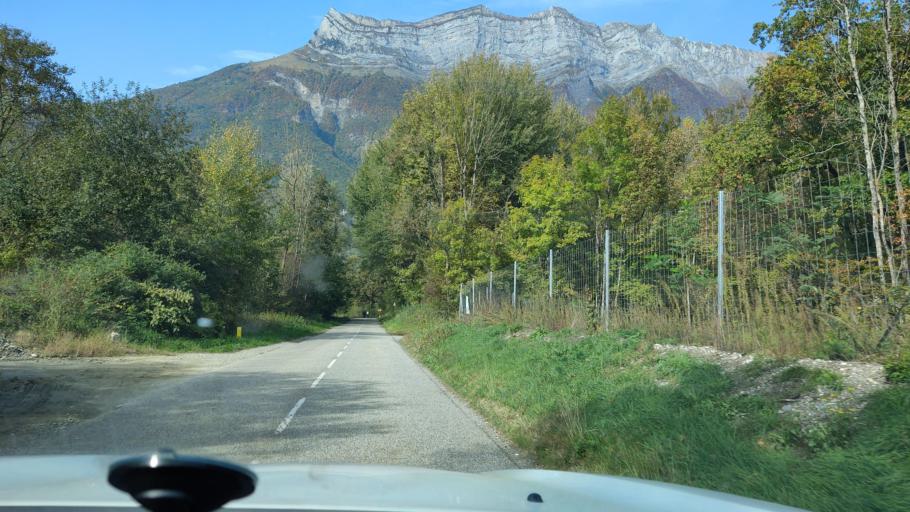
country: FR
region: Rhone-Alpes
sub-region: Departement de la Savoie
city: Aiton
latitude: 45.5662
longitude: 6.1962
